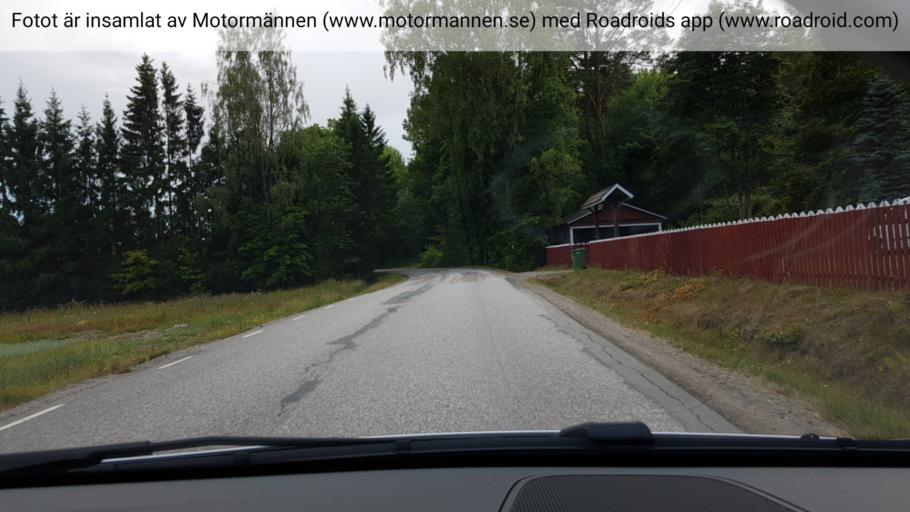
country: SE
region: Stockholm
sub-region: Nynashamns Kommun
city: Osmo
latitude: 59.0786
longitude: 17.8794
